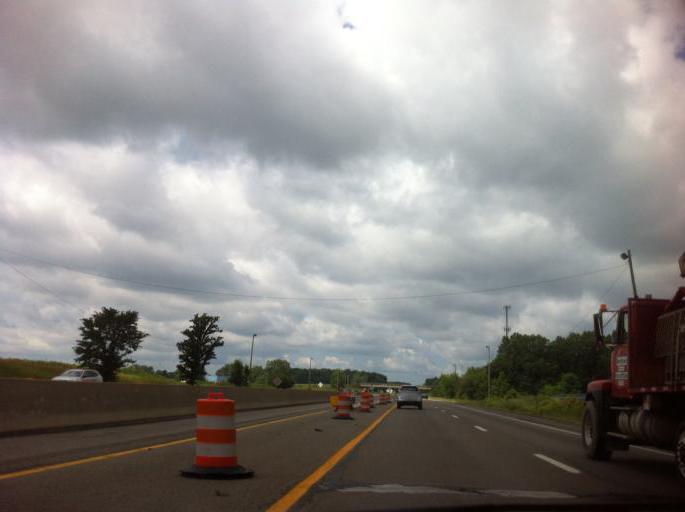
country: US
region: Ohio
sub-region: Lorain County
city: North Ridgeville
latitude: 41.3794
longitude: -82.0358
